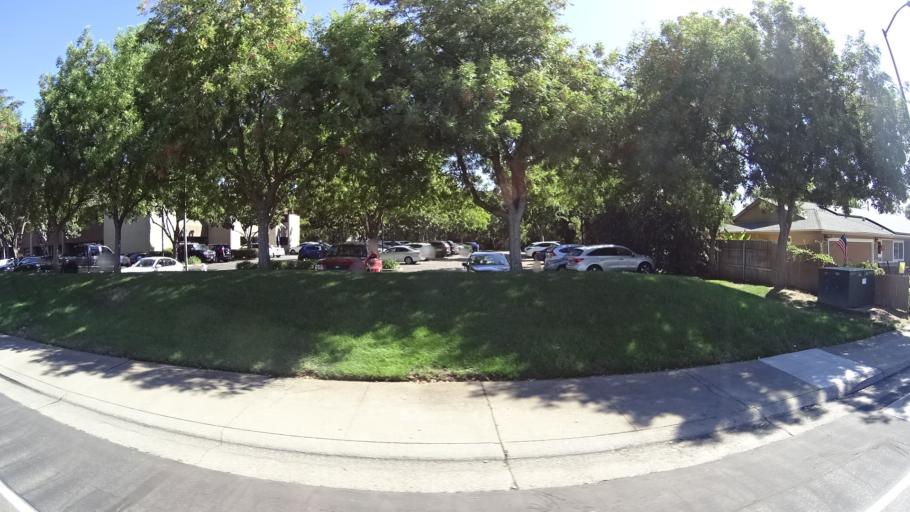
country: US
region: California
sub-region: Sacramento County
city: Elk Grove
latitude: 38.4039
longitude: -121.3714
